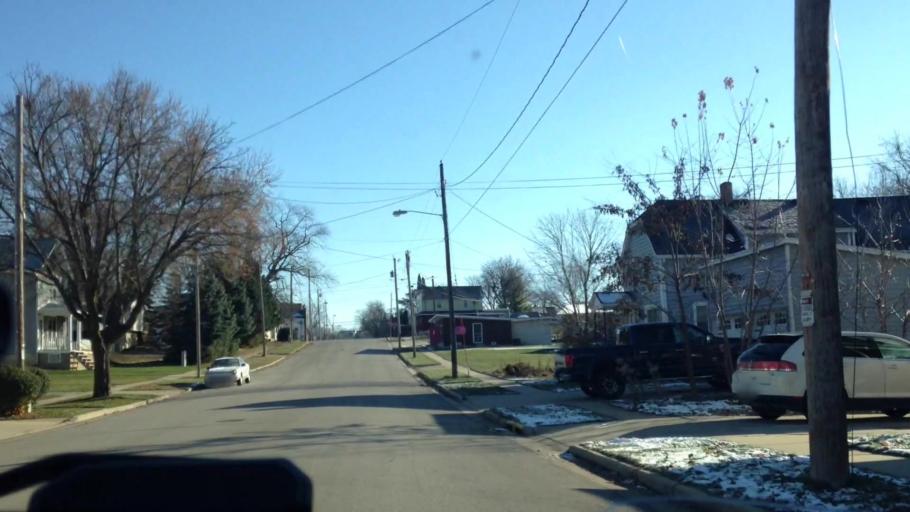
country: US
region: Wisconsin
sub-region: Dodge County
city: Mayville
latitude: 43.4976
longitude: -88.5504
